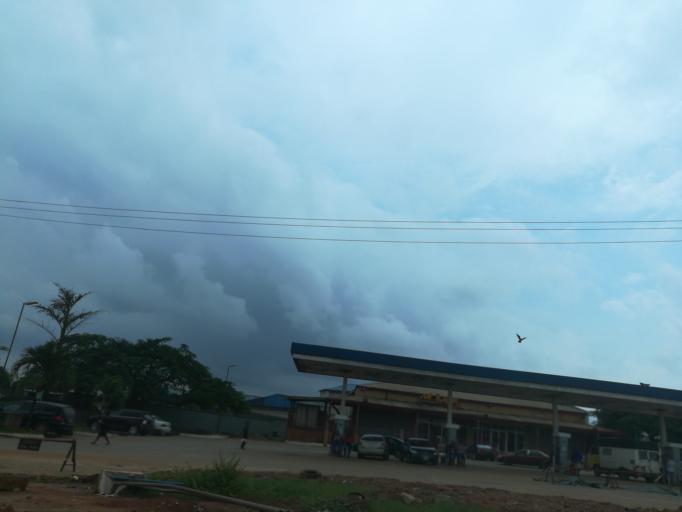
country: NG
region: Lagos
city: Oshodi
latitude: 6.5548
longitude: 3.3243
